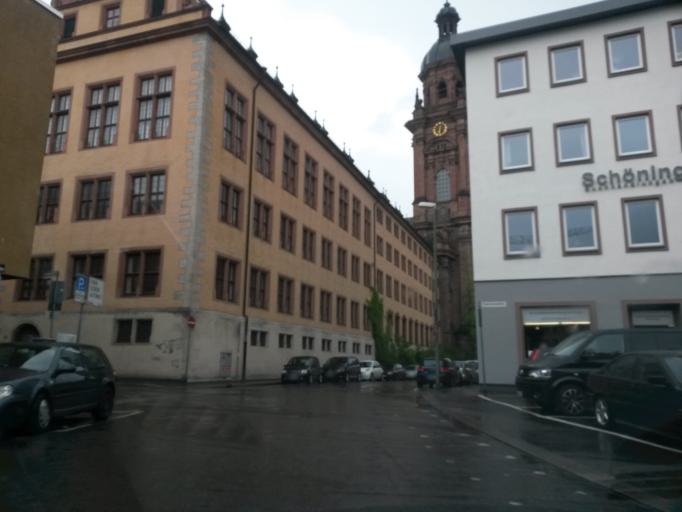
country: DE
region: Bavaria
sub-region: Regierungsbezirk Unterfranken
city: Wuerzburg
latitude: 49.7913
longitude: 9.9318
